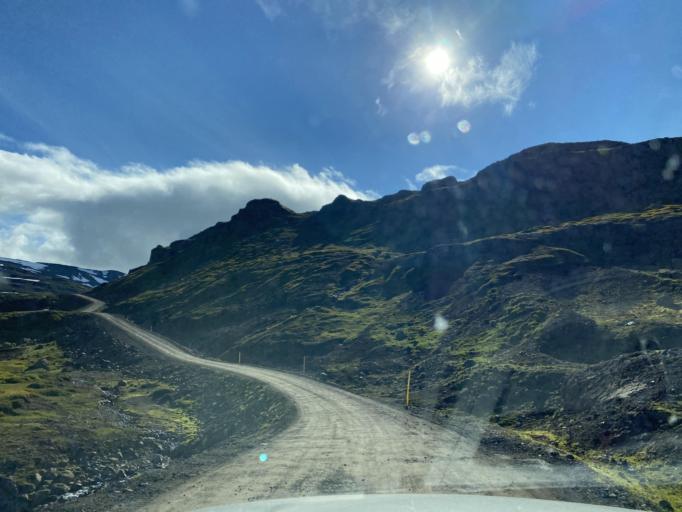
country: IS
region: East
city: Eskifjoerdur
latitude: 65.1767
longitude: -14.1108
